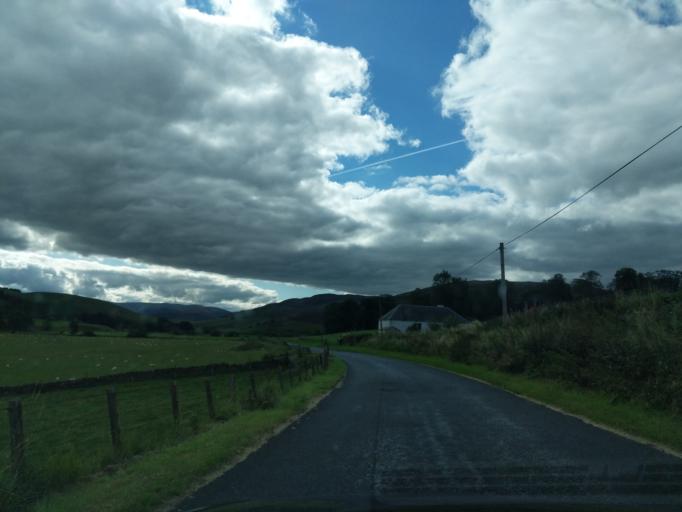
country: GB
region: Scotland
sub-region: The Scottish Borders
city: West Linton
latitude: 55.6806
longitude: -3.3333
